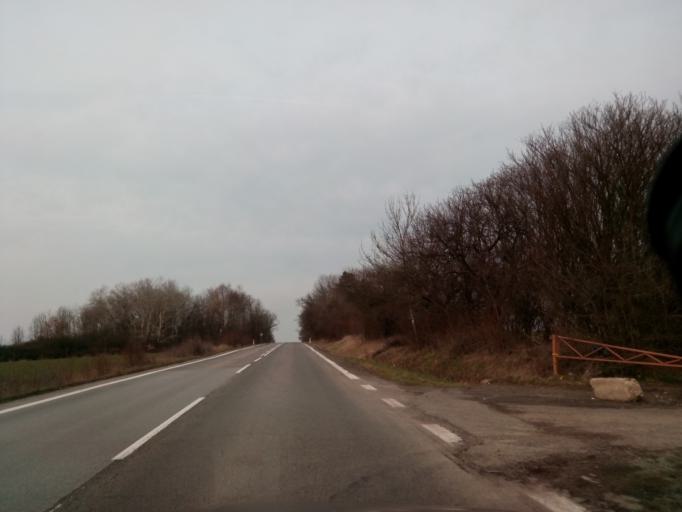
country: HU
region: Borsod-Abauj-Zemplen
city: Satoraljaujhely
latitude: 48.5066
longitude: 21.6549
